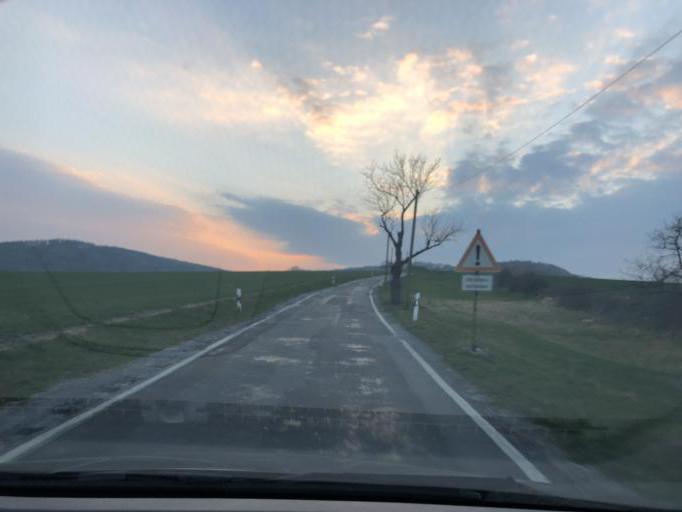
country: DE
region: Saxony
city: Elstra
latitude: 51.2356
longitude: 14.1264
